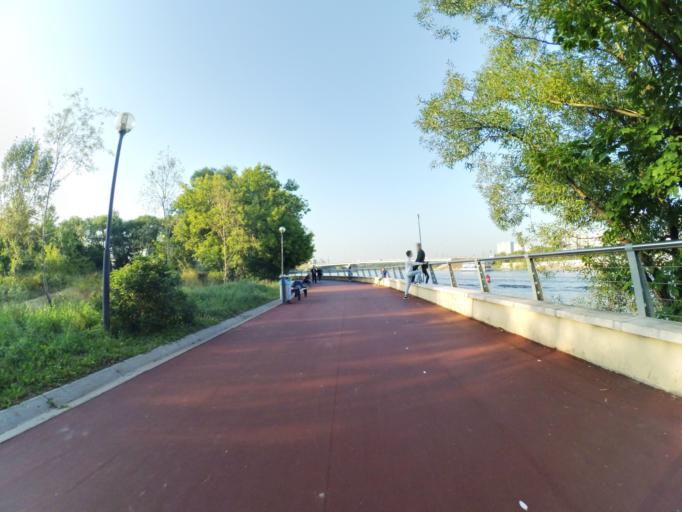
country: RU
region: Moskovskaya
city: Levoberezhnaya
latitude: 55.8684
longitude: 37.4529
